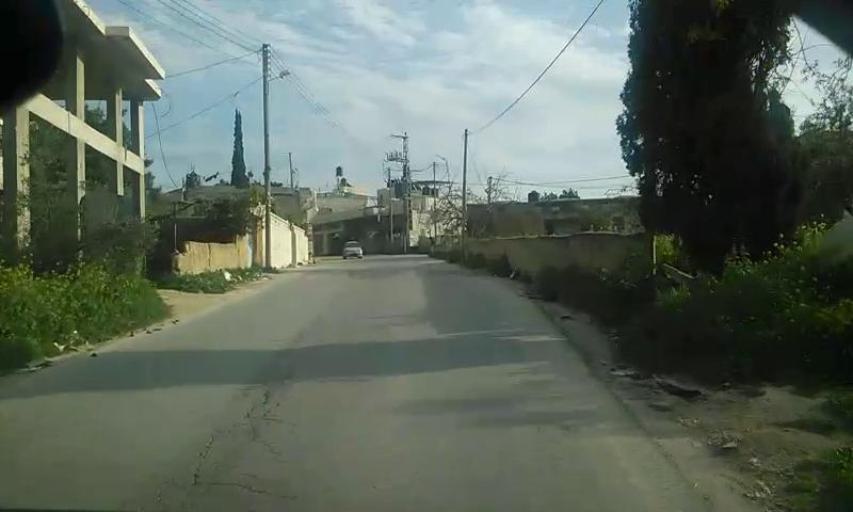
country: PS
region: West Bank
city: Nuba
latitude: 31.6103
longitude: 35.0344
